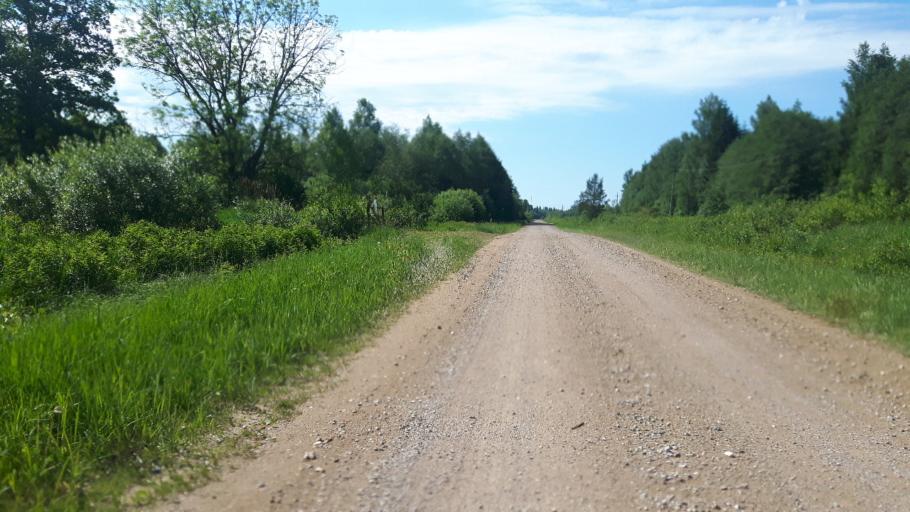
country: EE
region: Paernumaa
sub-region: Vaendra vald (alev)
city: Vandra
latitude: 58.6789
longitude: 25.0321
